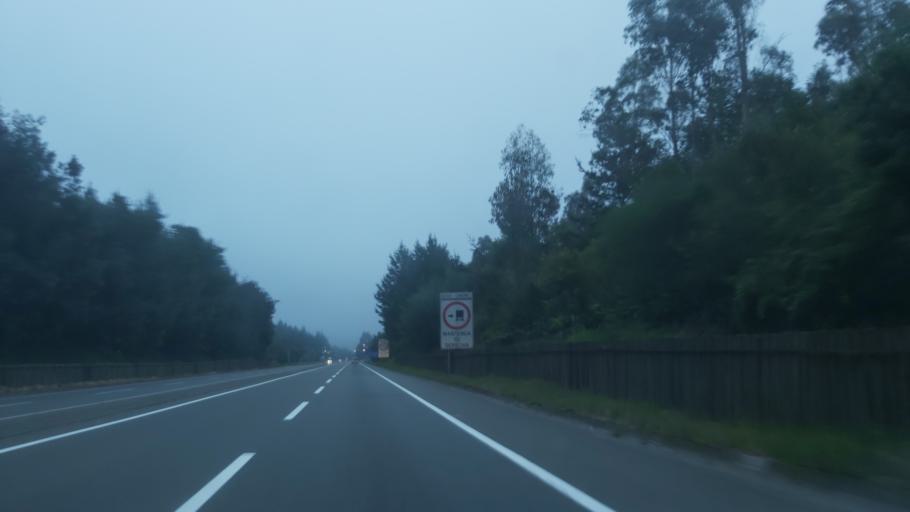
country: CL
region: Biobio
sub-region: Provincia de Concepcion
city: Penco
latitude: -36.7325
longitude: -72.8823
